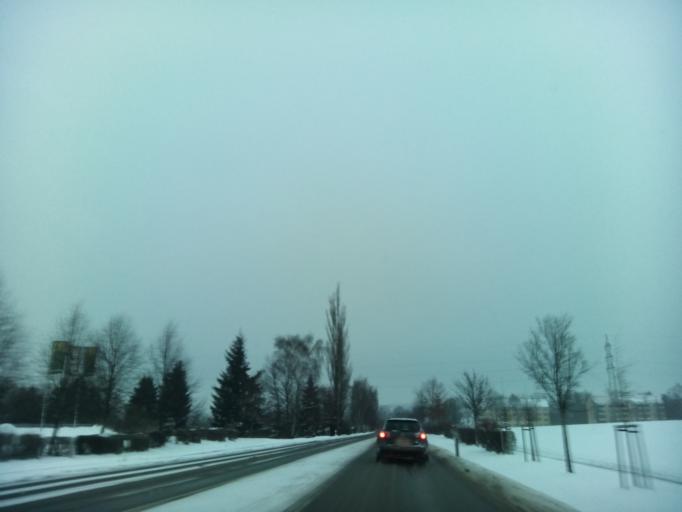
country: DE
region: Saxony
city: Freiberg
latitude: 50.8951
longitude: 13.3331
